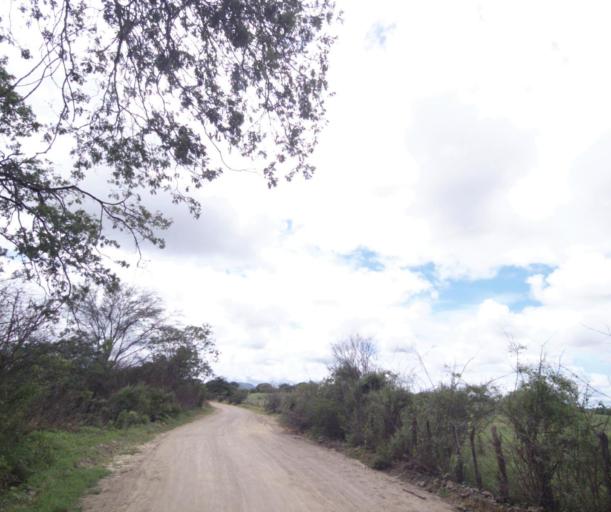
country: BR
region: Bahia
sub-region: Tanhacu
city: Tanhacu
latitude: -14.1642
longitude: -41.1707
